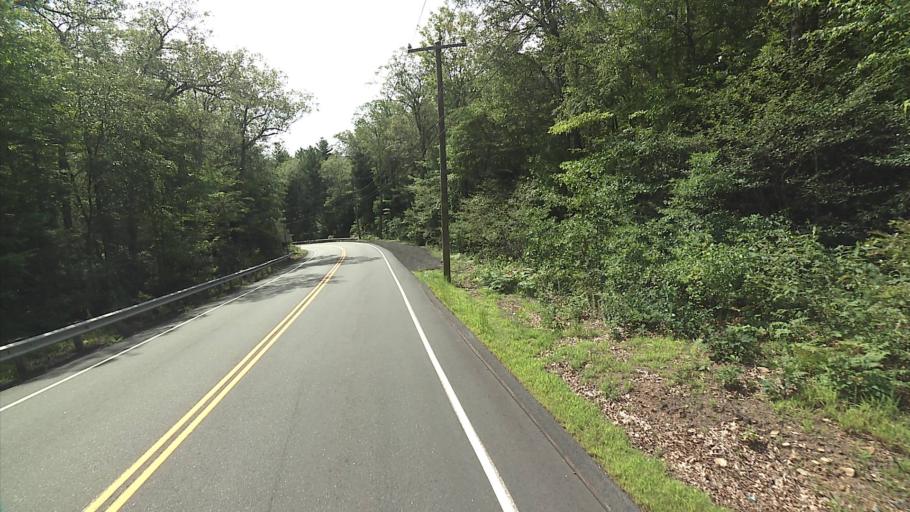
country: US
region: Massachusetts
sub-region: Hampden County
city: Holland
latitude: 41.9943
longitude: -72.1480
